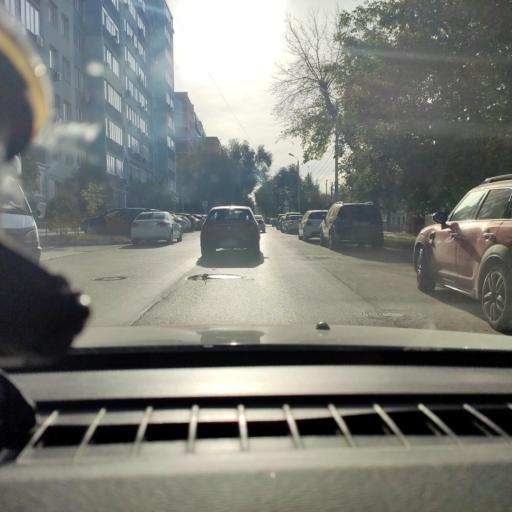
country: RU
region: Samara
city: Samara
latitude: 53.2024
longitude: 50.1216
